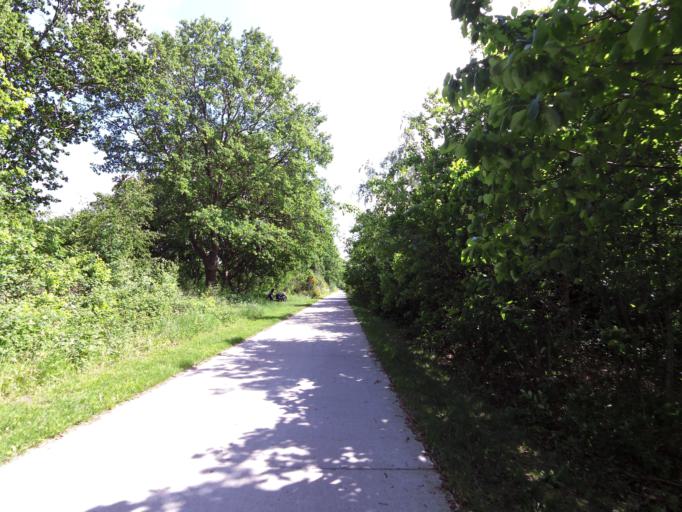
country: BE
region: Flanders
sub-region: Provincie West-Vlaanderen
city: Beernem
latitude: 51.1306
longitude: 3.3420
